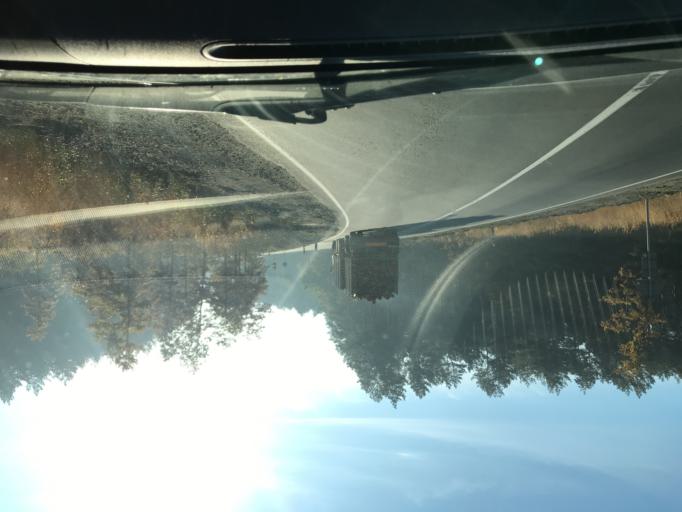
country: BY
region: Brest
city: Luninyets
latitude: 52.2825
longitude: 26.8269
